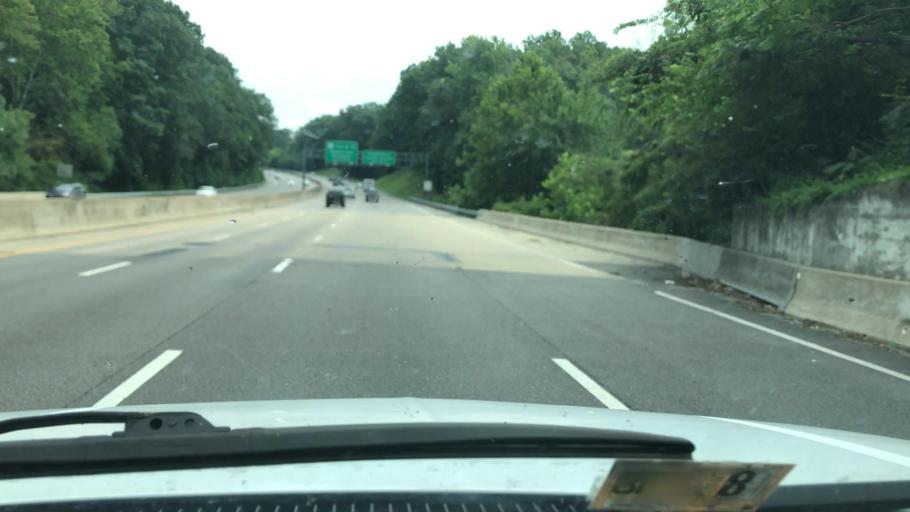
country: US
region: Virginia
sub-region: Chesterfield County
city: Bensley
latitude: 37.4579
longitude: -77.4956
